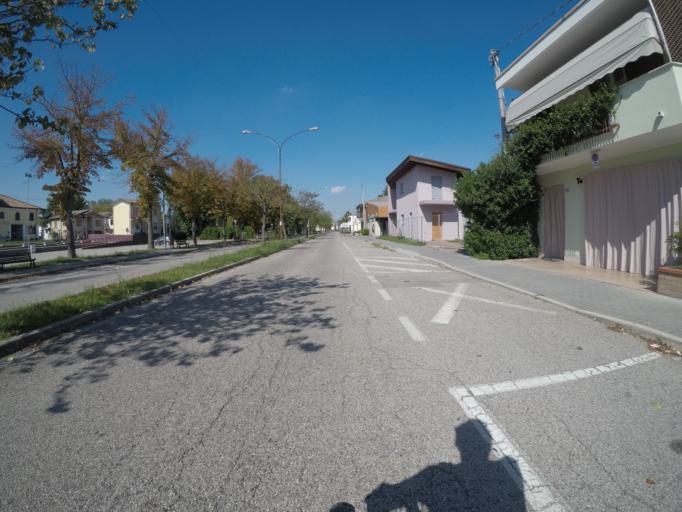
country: IT
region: Veneto
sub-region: Provincia di Rovigo
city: Polesella
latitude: 44.9622
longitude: 11.7512
